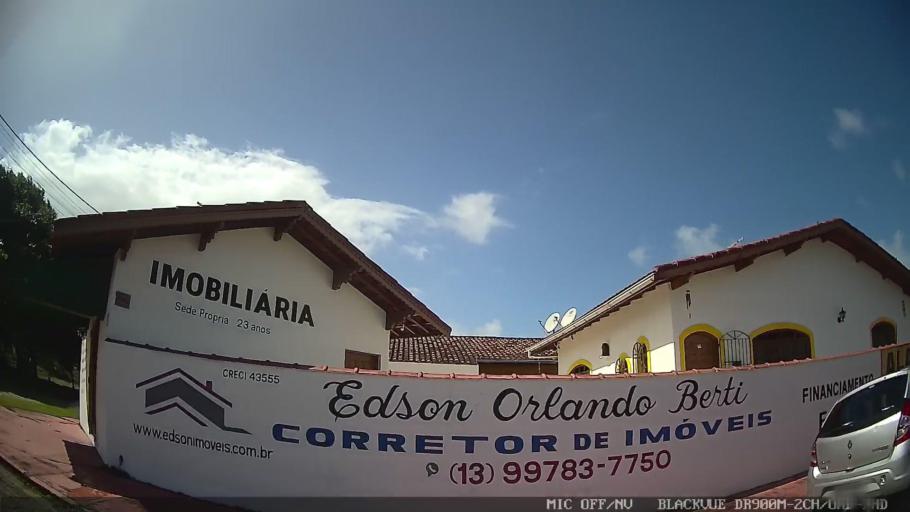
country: BR
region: Sao Paulo
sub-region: Itanhaem
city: Itanhaem
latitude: -24.1683
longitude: -46.7615
